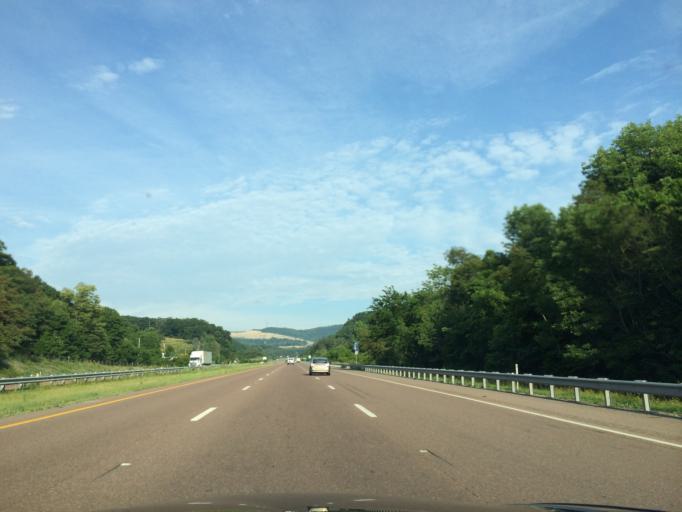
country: US
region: Maryland
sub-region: Allegany County
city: Cumberland
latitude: 39.7065
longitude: -78.5768
